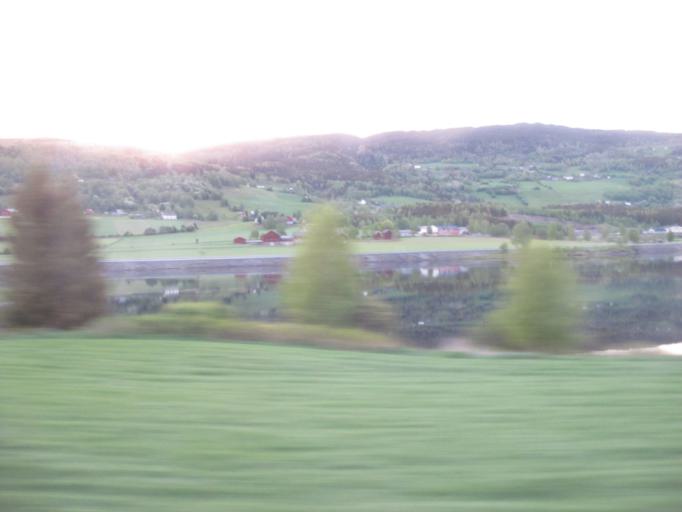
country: NO
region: Oppland
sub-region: Oyer
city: Tretten
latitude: 61.2563
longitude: 10.4183
